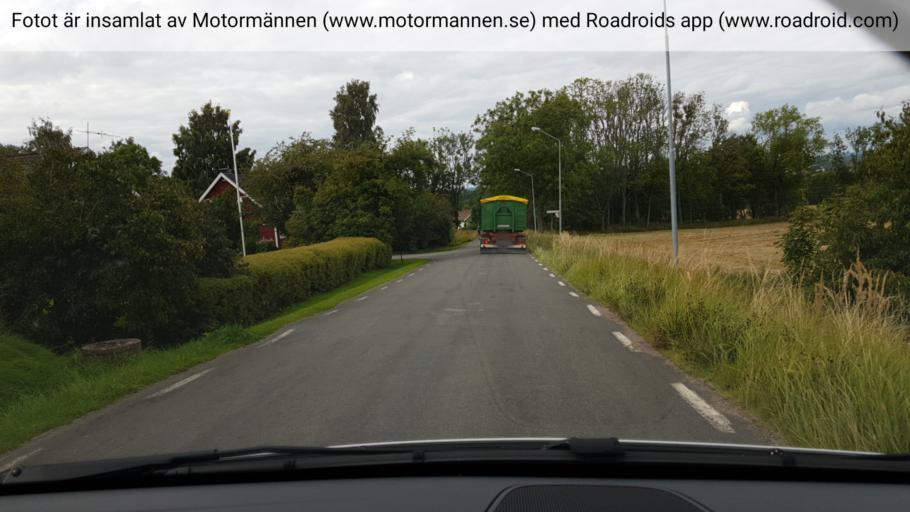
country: SE
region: Vaestra Goetaland
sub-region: Skovde Kommun
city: Skultorp
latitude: 58.2259
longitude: 13.8130
